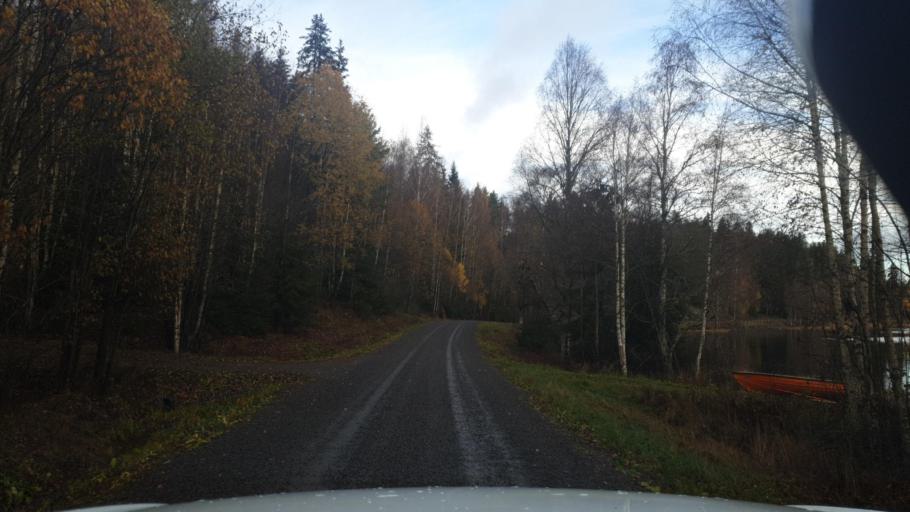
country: NO
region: Hedmark
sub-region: Eidskog
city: Skotterud
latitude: 59.8818
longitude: 11.9766
